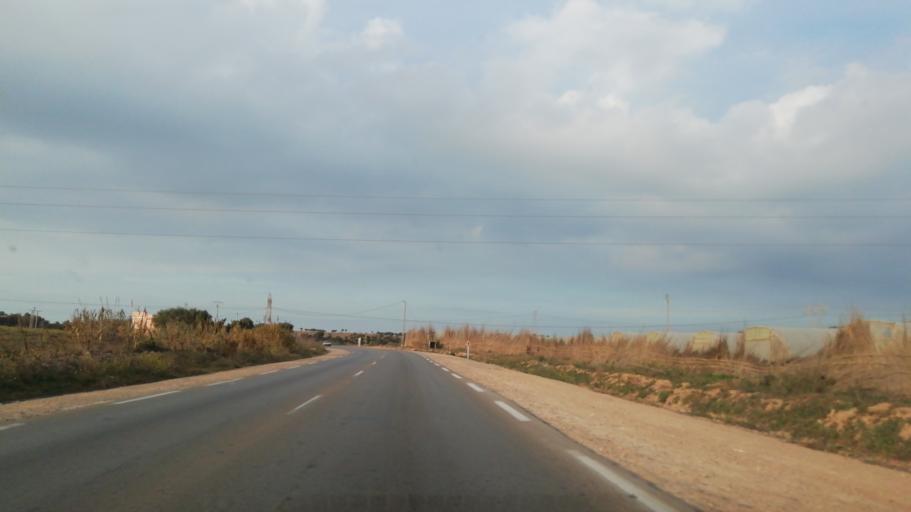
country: DZ
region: Oran
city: Ain el Bya
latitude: 35.7783
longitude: -0.0973
